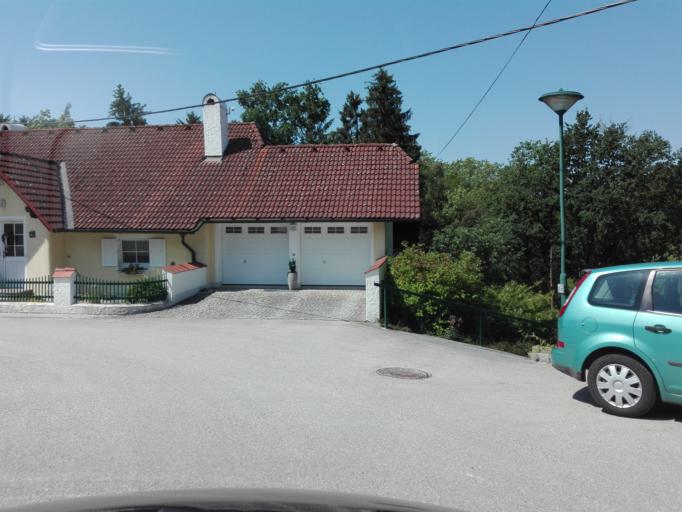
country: AT
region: Upper Austria
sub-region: Politischer Bezirk Urfahr-Umgebung
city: Engerwitzdorf
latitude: 48.2852
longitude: 14.4709
